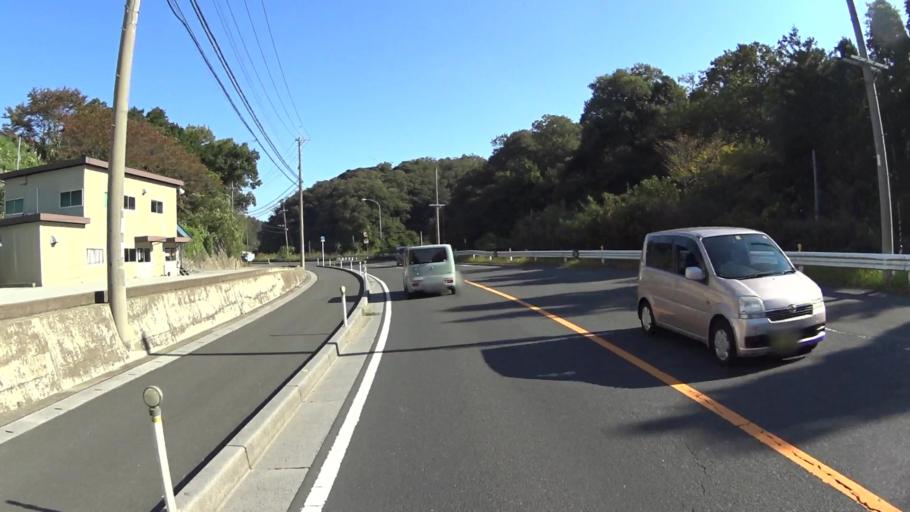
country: JP
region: Kyoto
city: Miyazu
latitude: 35.6506
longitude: 135.0374
